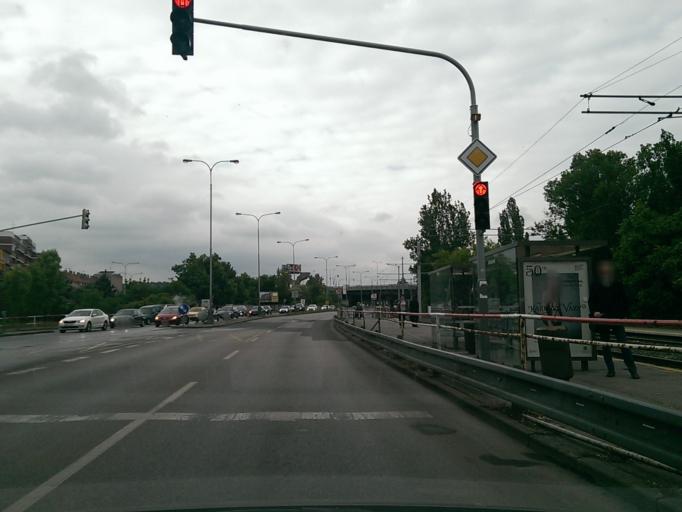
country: CZ
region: Praha
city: Branik
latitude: 50.0403
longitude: 14.4096
